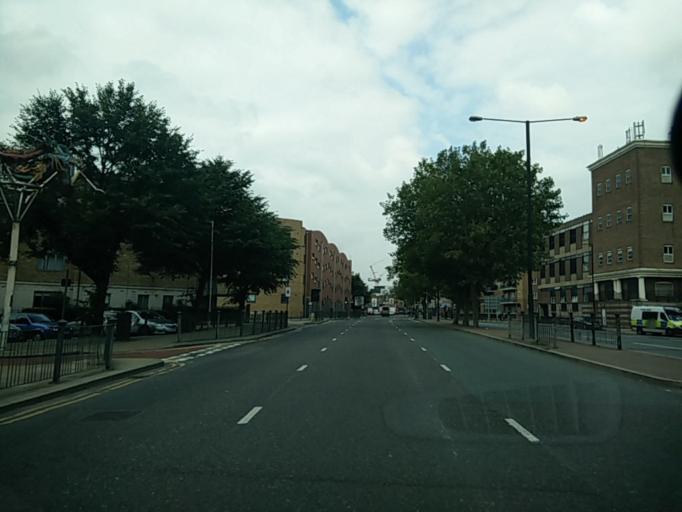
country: GB
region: England
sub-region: Greater London
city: Poplar
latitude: 51.5100
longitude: -0.0262
